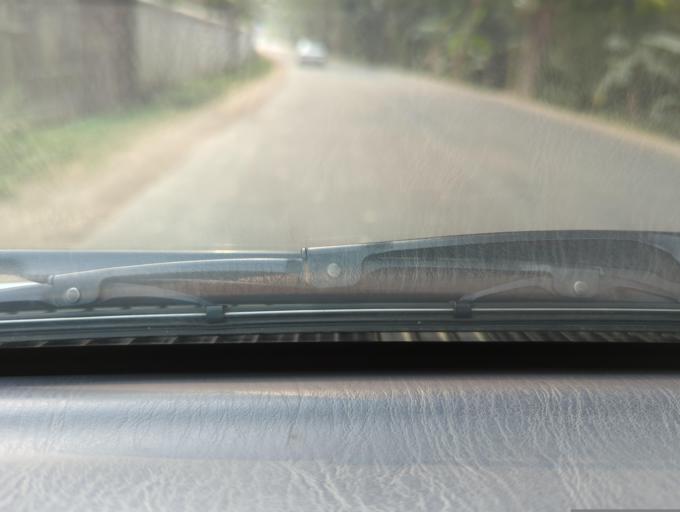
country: BD
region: Sylhet
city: Maulavi Bazar
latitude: 24.5240
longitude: 91.7313
